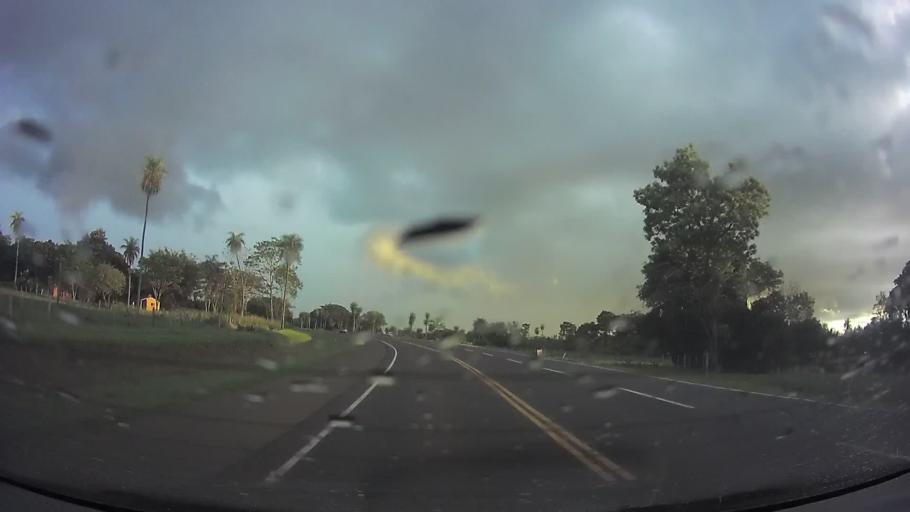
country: PY
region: Paraguari
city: Paraguari
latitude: -25.6096
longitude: -57.1850
